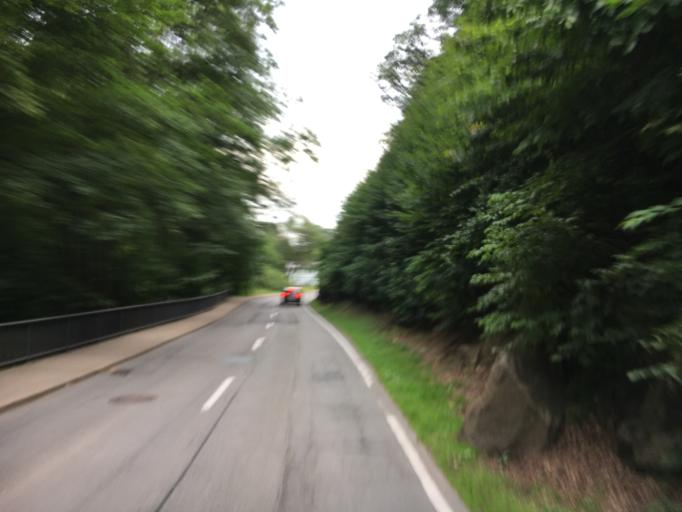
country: DE
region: Thuringia
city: Trusetal
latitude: 50.7925
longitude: 10.4134
